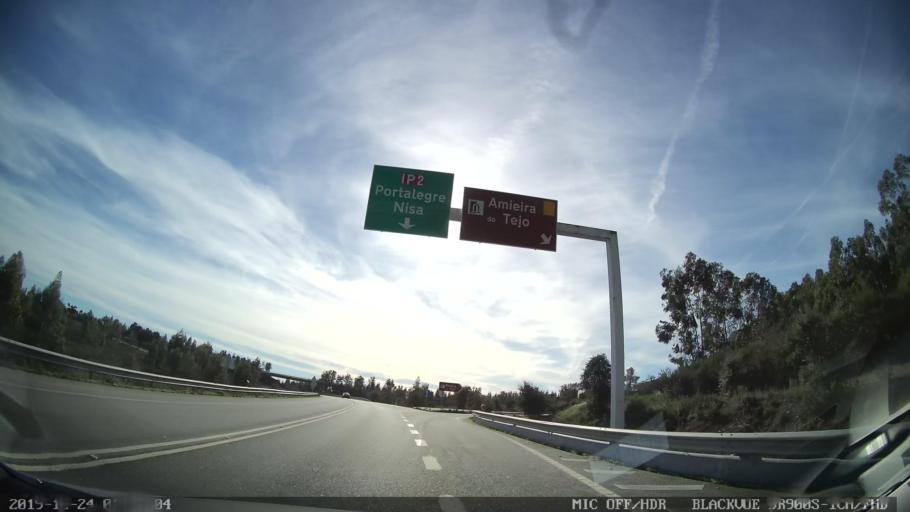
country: PT
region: Portalegre
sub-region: Nisa
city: Nisa
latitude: 39.4998
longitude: -7.7686
